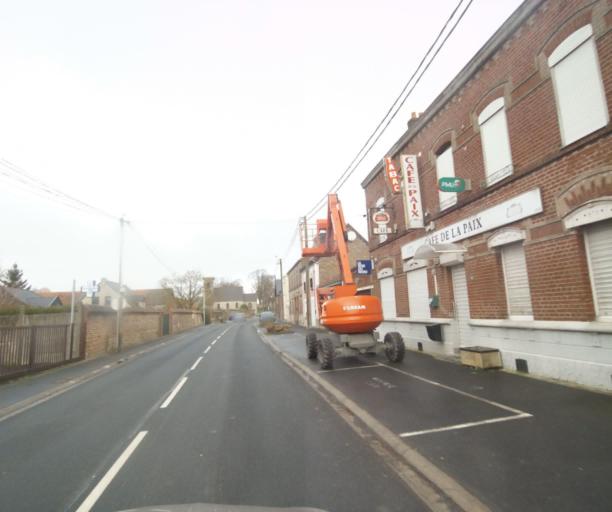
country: FR
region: Nord-Pas-de-Calais
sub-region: Departement du Nord
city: Vendegies-sur-Ecaillon
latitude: 50.2854
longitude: 3.5133
